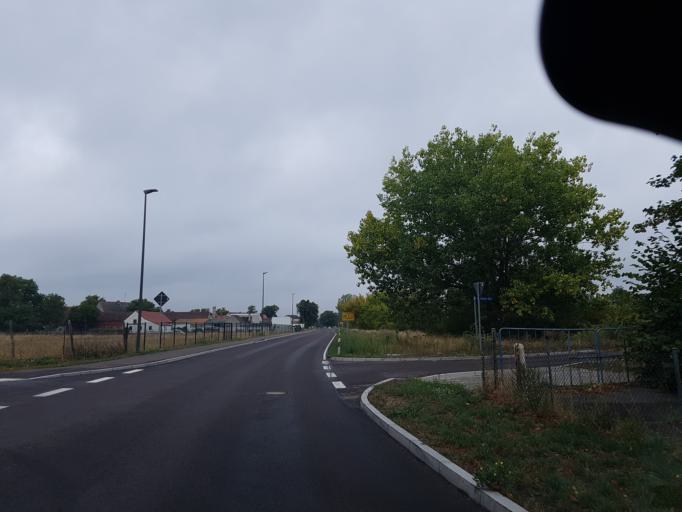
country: DE
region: Brandenburg
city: Ziesar
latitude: 52.2666
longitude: 12.2971
